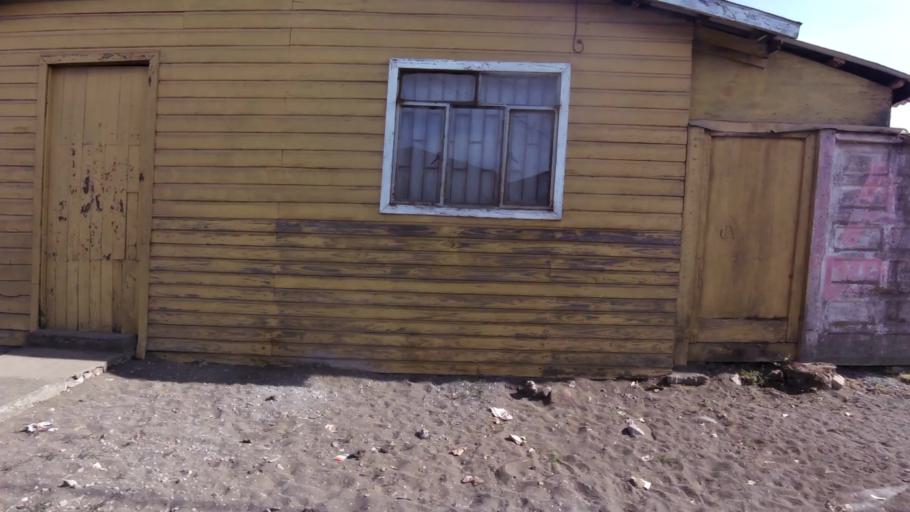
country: CL
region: Biobio
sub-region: Provincia de Concepcion
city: Talcahuano
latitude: -36.7792
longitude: -73.1149
